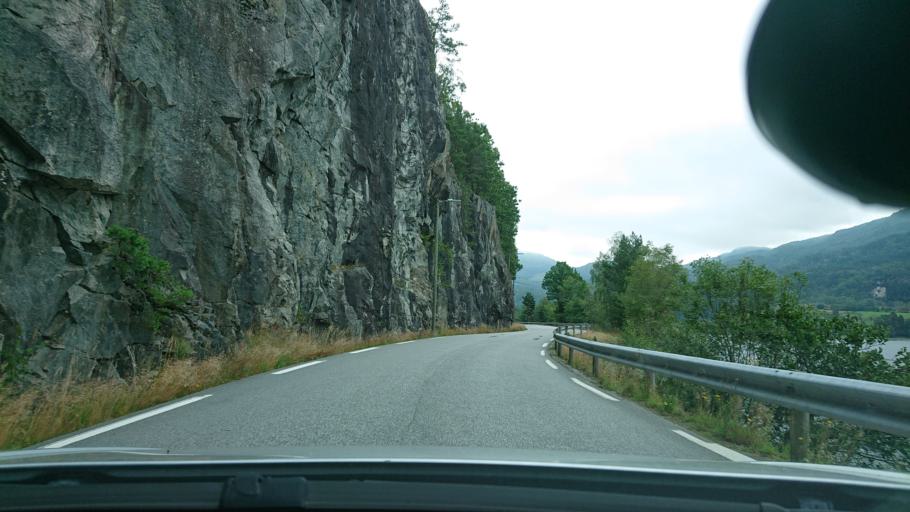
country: NO
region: Rogaland
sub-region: Hjelmeland
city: Hjelmelandsvagen
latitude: 59.2315
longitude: 6.1916
